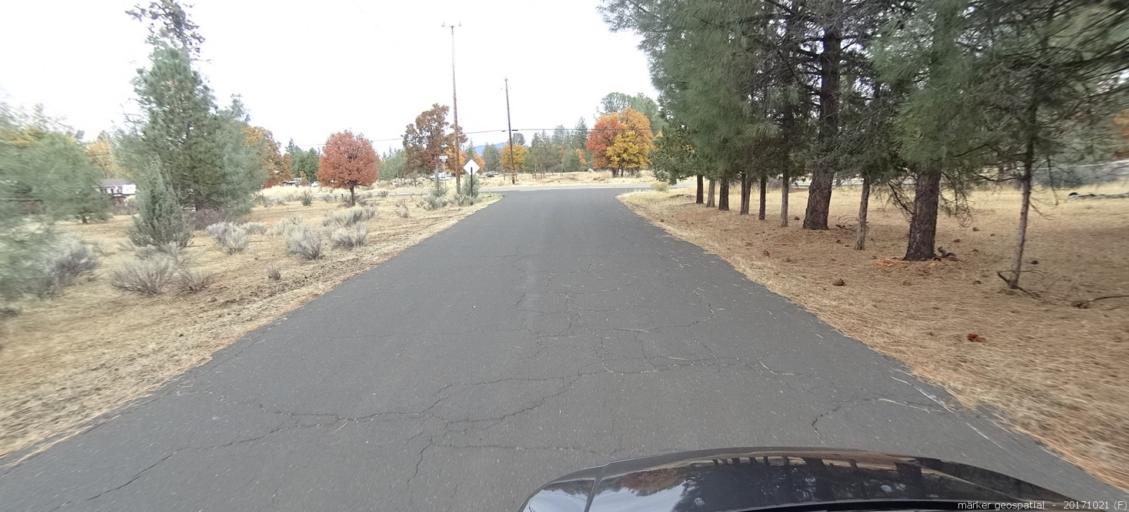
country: US
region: California
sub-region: Shasta County
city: Burney
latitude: 40.9185
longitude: -121.5497
